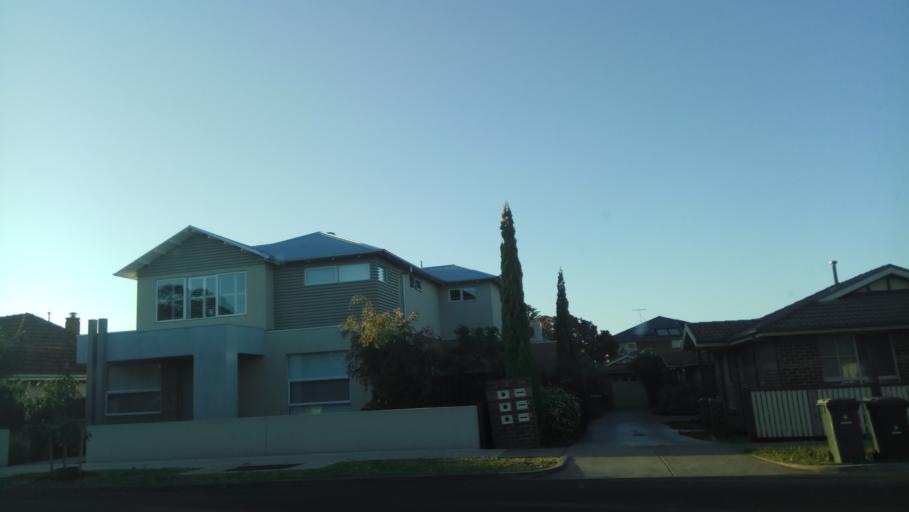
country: AU
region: Victoria
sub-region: Hobsons Bay
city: Altona
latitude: -37.8696
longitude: 144.8162
